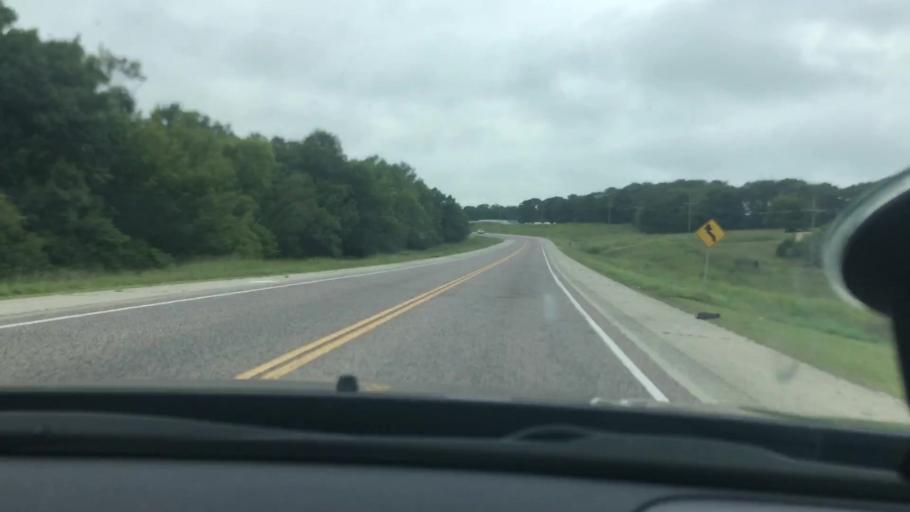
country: US
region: Oklahoma
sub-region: Pontotoc County
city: Ada
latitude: 34.7877
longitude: -96.5673
